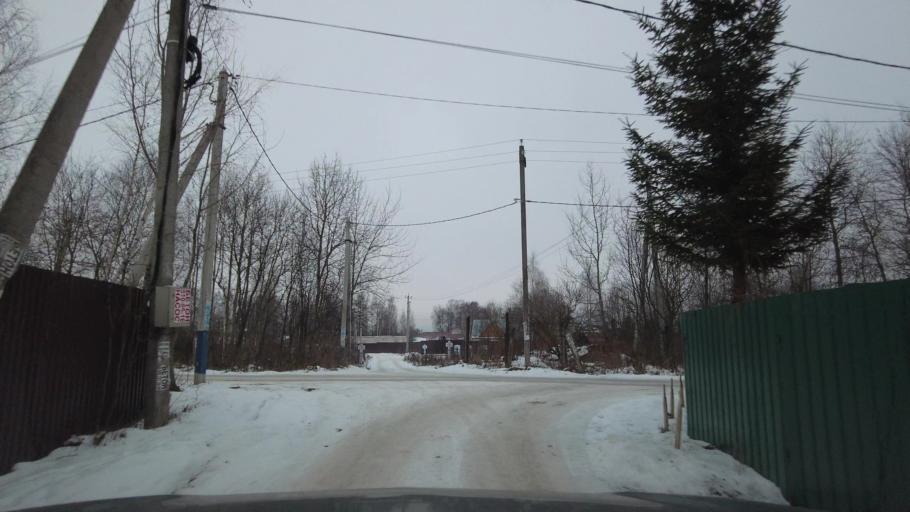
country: RU
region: Moskovskaya
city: Novopodrezkovo
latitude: 55.9862
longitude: 37.3918
